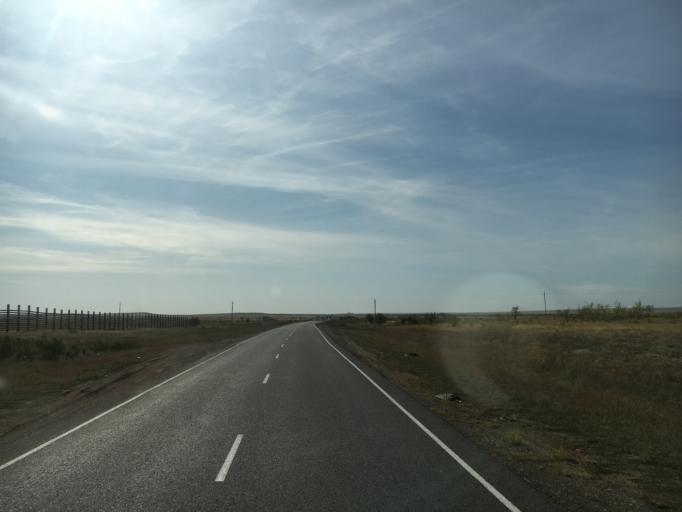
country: KZ
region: Batys Qazaqstan
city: Kamenka
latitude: 51.1087
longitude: 50.4429
